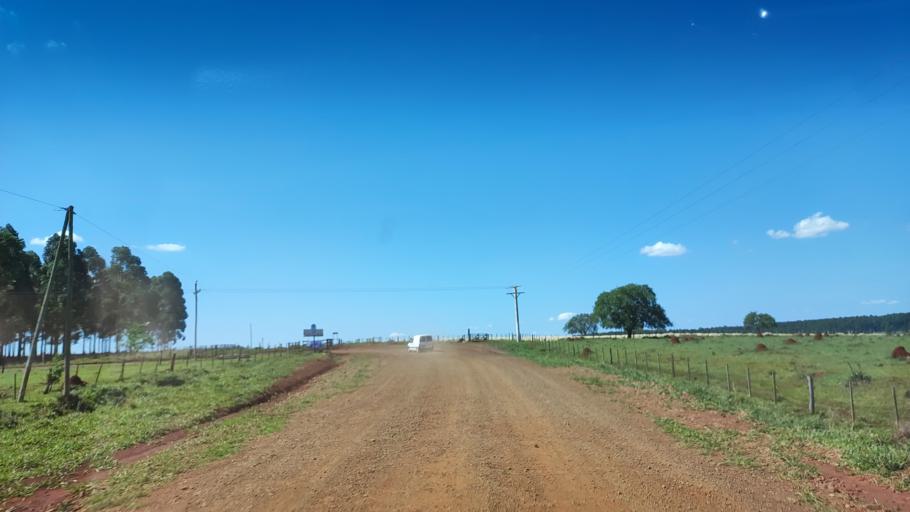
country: PY
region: Itapua
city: San Juan del Parana
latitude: -27.4230
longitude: -56.0803
